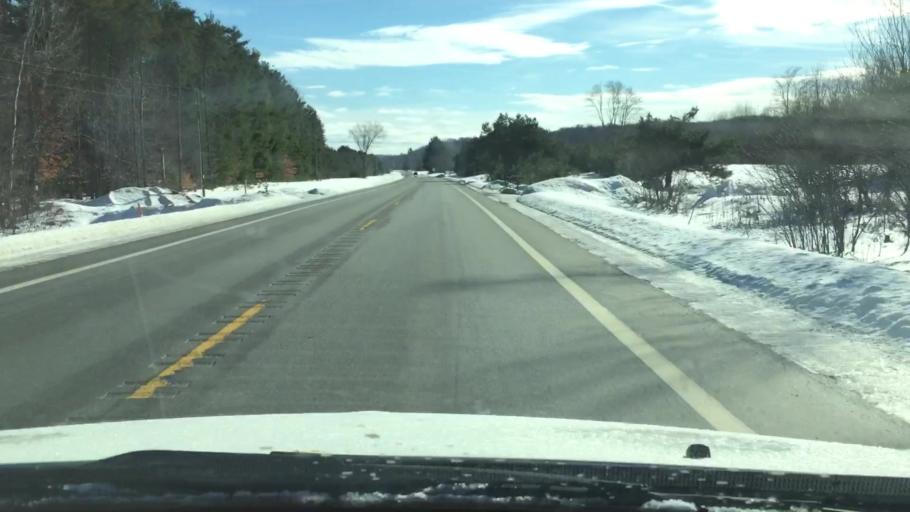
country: US
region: Michigan
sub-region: Charlevoix County
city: East Jordan
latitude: 45.0765
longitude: -85.0878
